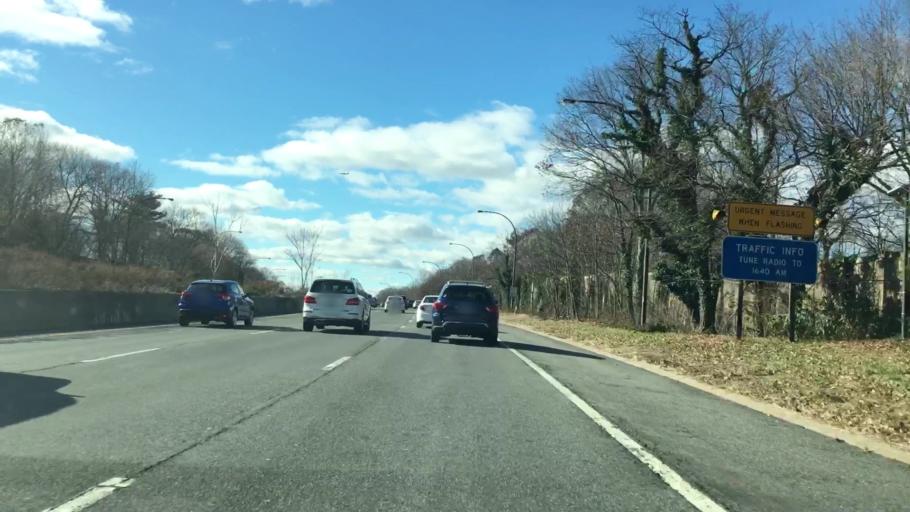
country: US
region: New York
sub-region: Nassau County
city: New Cassel
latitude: 40.7664
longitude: -73.5785
